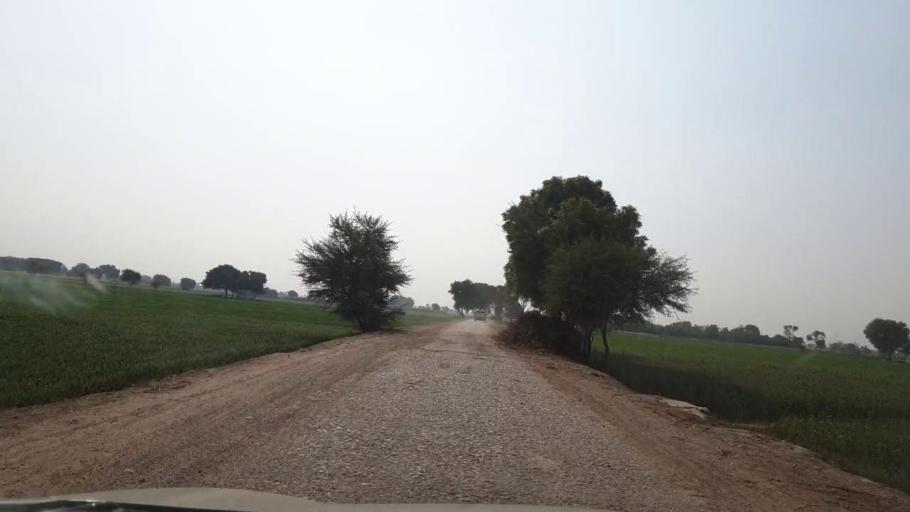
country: PK
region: Sindh
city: Bhit Shah
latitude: 25.7501
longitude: 68.4955
